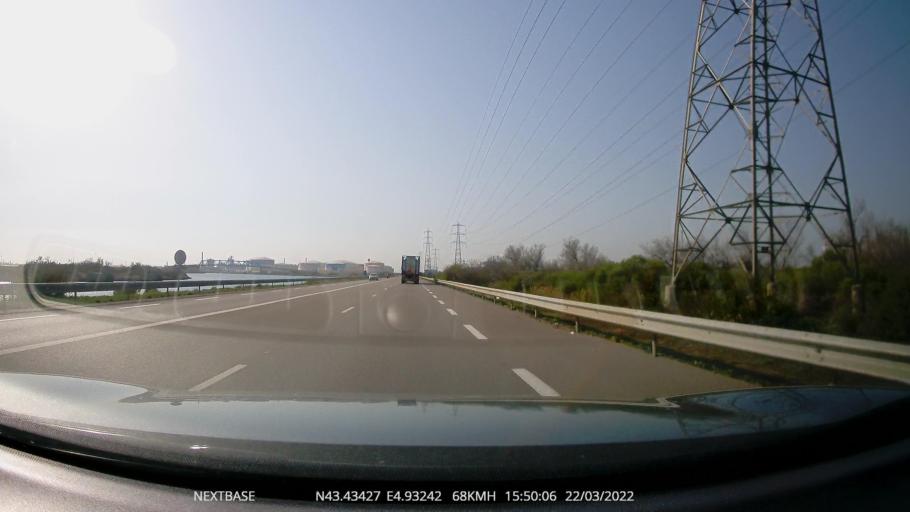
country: FR
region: Provence-Alpes-Cote d'Azur
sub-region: Departement des Bouches-du-Rhone
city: Fos-sur-Mer
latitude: 43.4343
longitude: 4.9323
